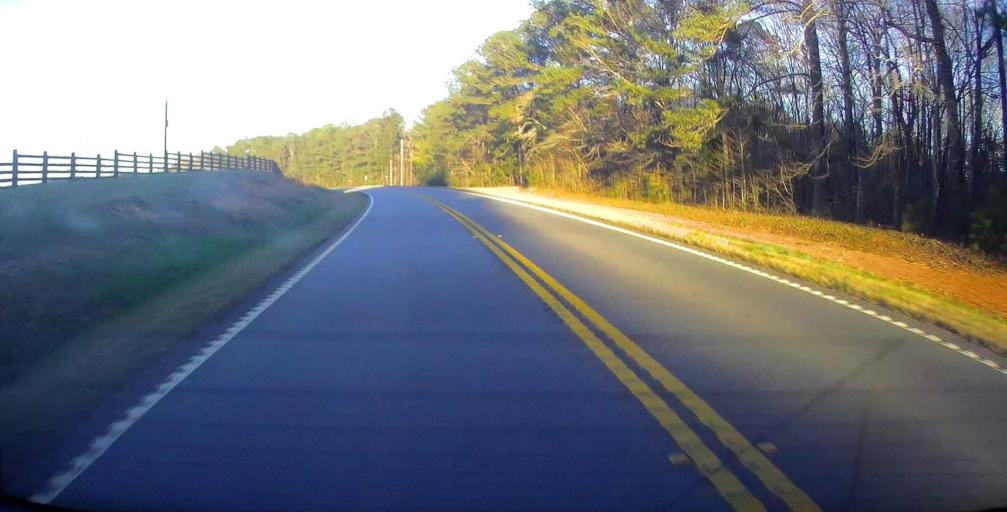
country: US
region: Alabama
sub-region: Lee County
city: Smiths Station
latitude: 32.6540
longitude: -85.0020
